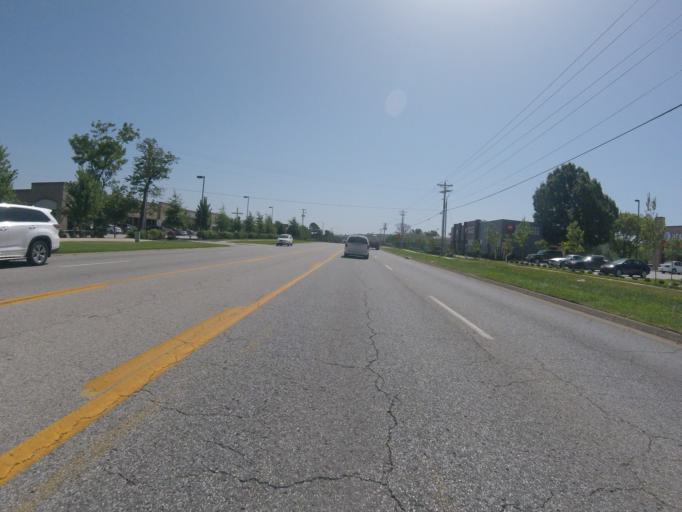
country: US
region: Arkansas
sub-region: Washington County
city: Farmington
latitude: 36.0783
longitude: -94.2111
